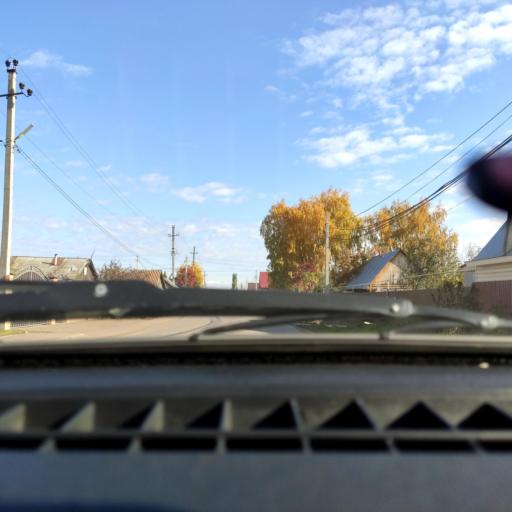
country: RU
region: Bashkortostan
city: Ufa
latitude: 54.6104
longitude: 55.9407
